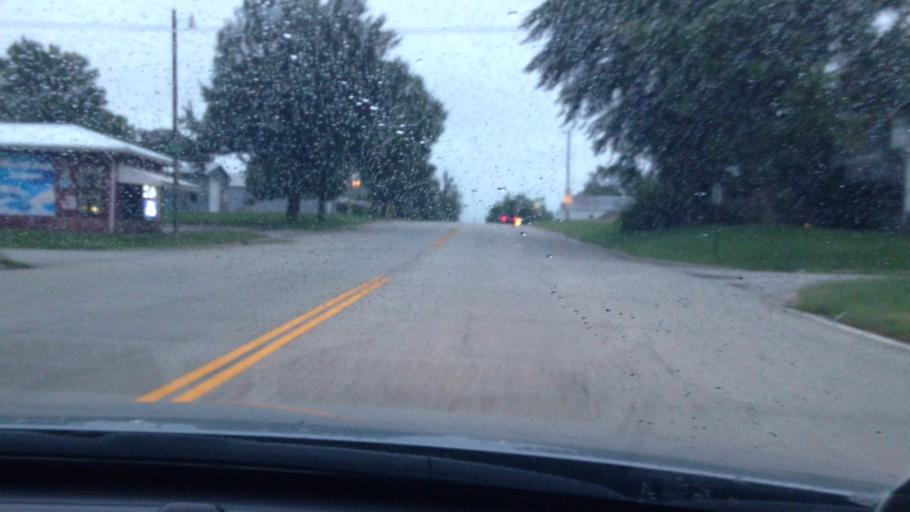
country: US
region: Kansas
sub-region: Brown County
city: Horton
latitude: 39.6729
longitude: -95.5273
